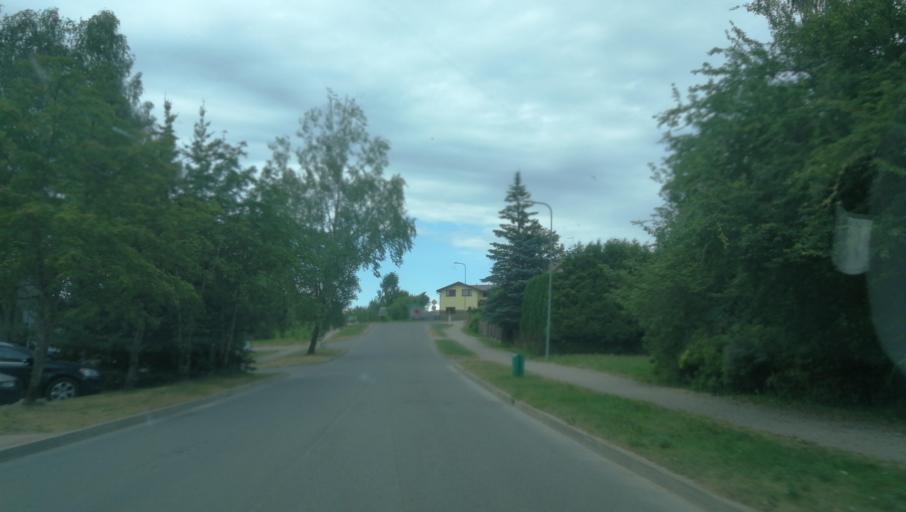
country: LV
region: Cesu Rajons
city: Cesis
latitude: 57.3080
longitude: 25.2951
